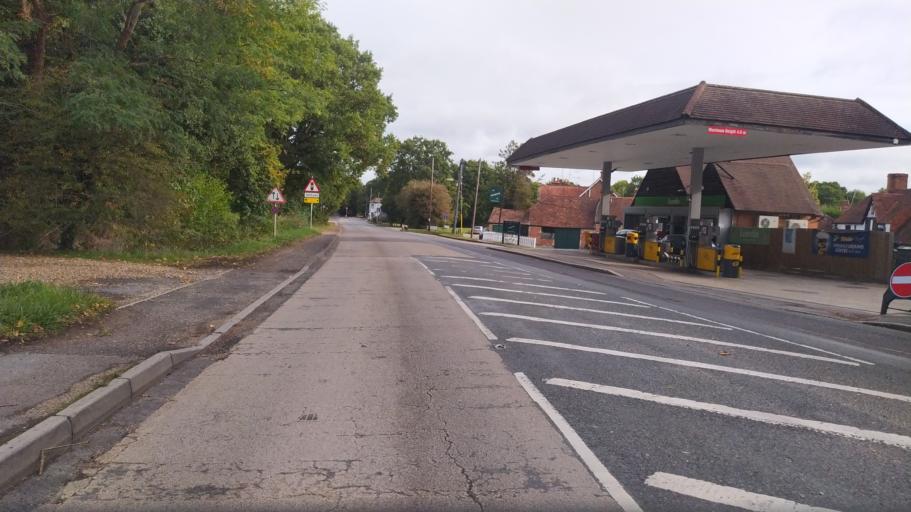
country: GB
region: England
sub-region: Hampshire
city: Hook
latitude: 51.2959
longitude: -0.9135
